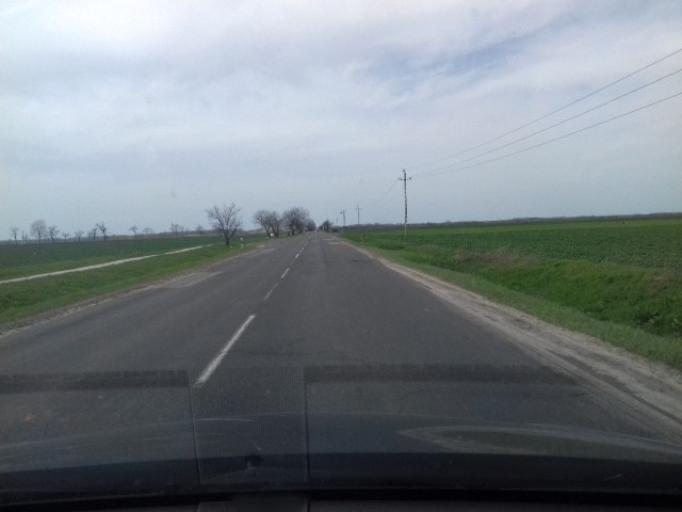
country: HU
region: Jasz-Nagykun-Szolnok
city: Kunszentmarton
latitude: 46.8514
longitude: 20.2465
